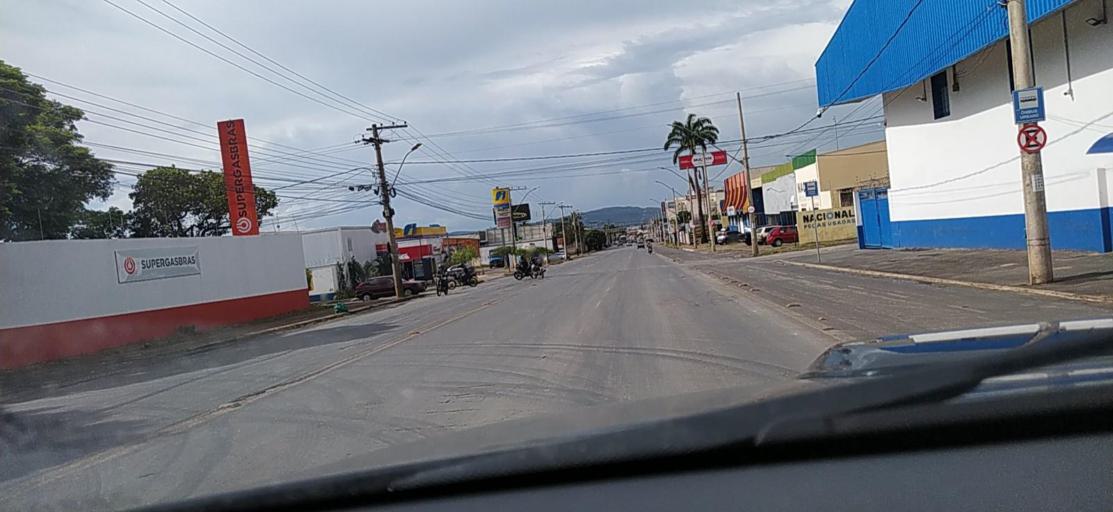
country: BR
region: Minas Gerais
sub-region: Montes Claros
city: Montes Claros
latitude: -16.7388
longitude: -43.8462
